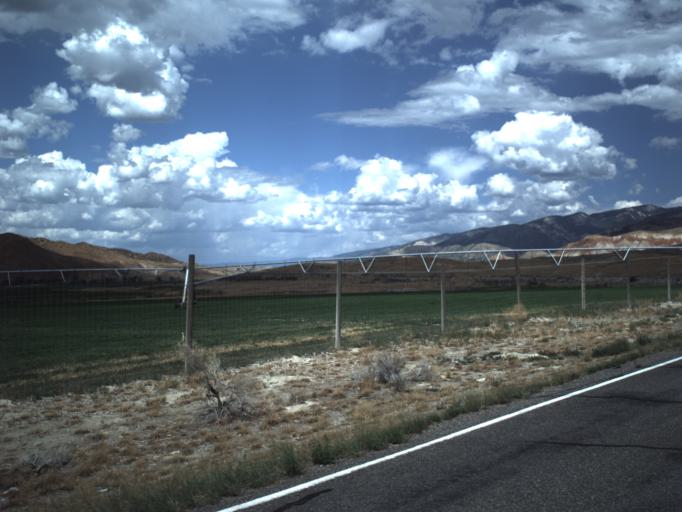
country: US
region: Utah
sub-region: Sanpete County
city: Gunnison
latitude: 39.1448
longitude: -111.7536
